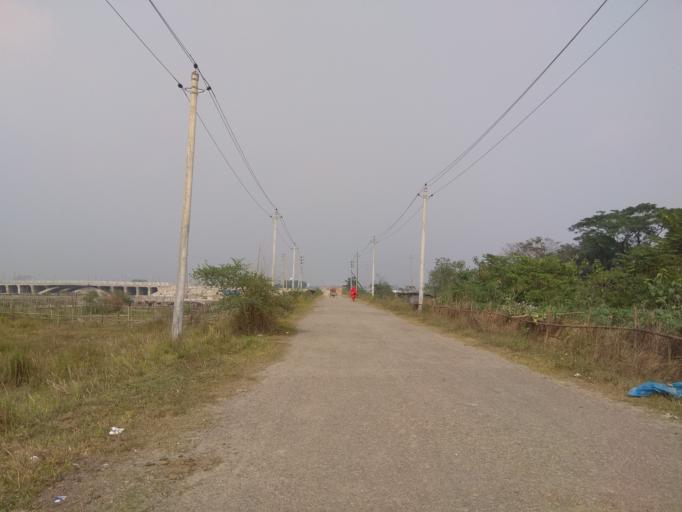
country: BD
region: Dhaka
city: Tungi
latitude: 23.8582
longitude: 90.3726
